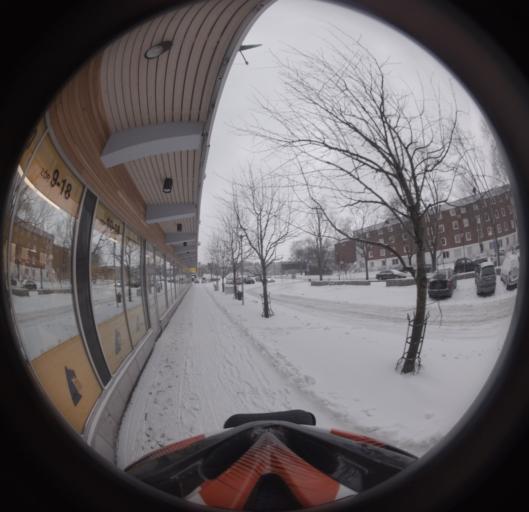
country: SE
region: Stockholm
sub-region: Sollentuna Kommun
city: Sollentuna
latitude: 59.4252
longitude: 17.9469
